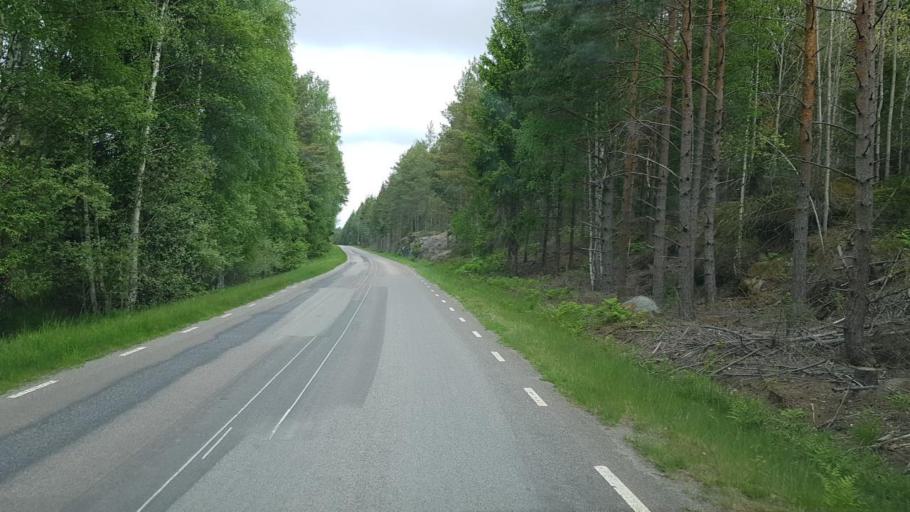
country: SE
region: OEstergoetland
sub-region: Linkopings Kommun
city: Ljungsbro
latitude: 58.6134
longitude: 15.4744
